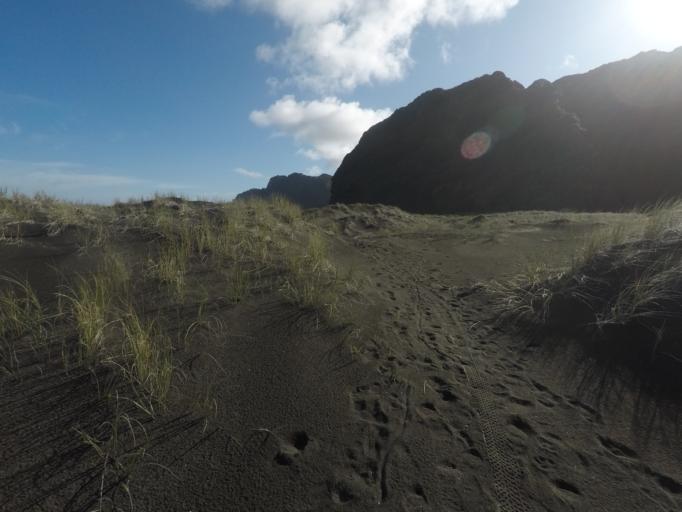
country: NZ
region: Auckland
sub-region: Auckland
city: Muriwai Beach
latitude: -36.9954
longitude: 174.4740
